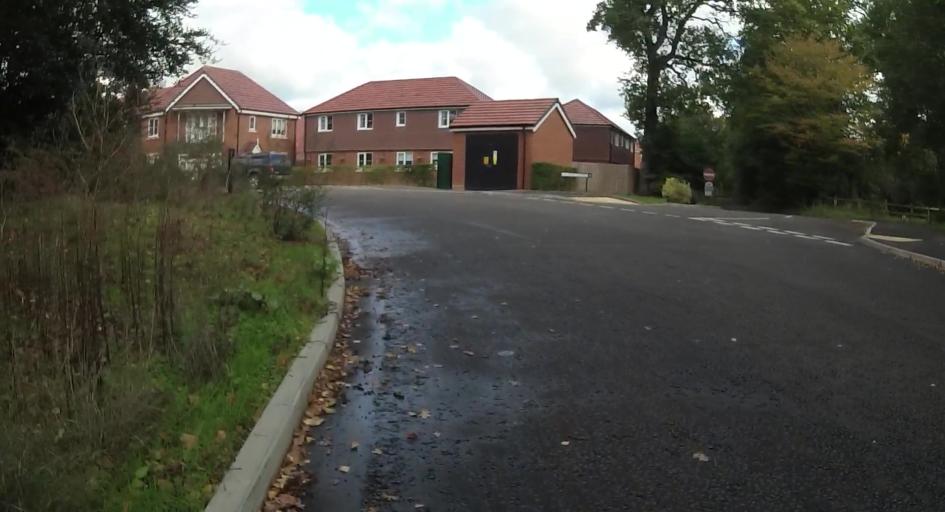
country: GB
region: England
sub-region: Hampshire
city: Fleet
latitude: 51.2929
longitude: -0.8683
